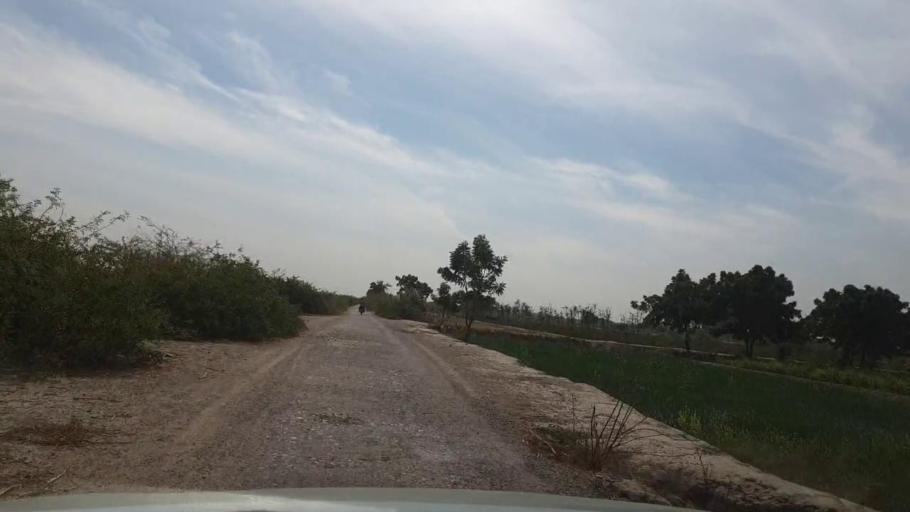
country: PK
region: Sindh
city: Nabisar
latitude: 25.0876
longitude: 69.5998
